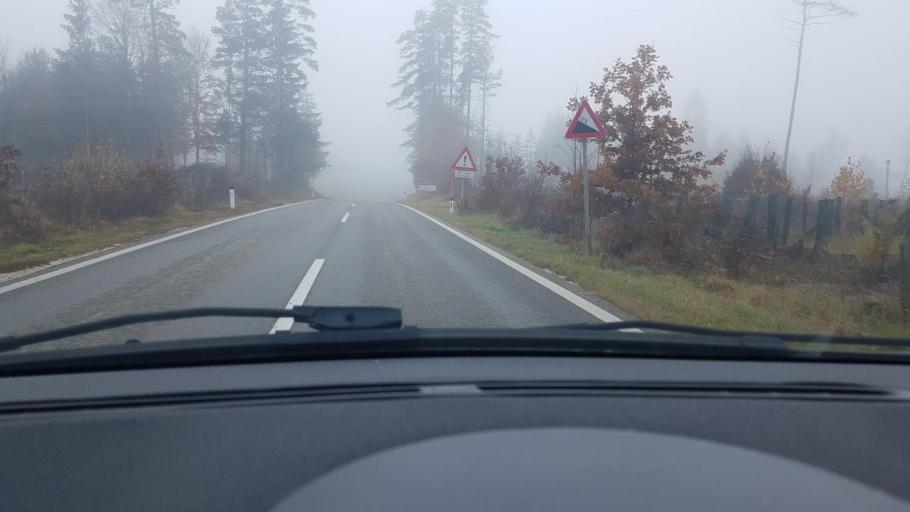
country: AT
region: Carinthia
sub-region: Politischer Bezirk Volkermarkt
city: Sittersdorf
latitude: 46.5474
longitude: 14.6198
